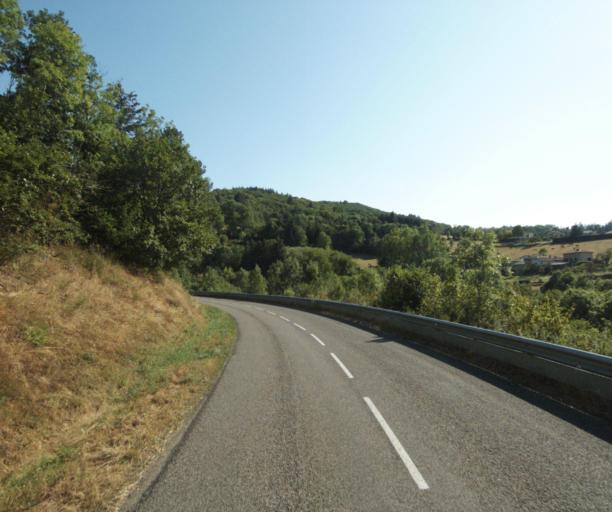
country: FR
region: Rhone-Alpes
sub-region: Departement du Rhone
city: Saint-Pierre-la-Palud
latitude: 45.7712
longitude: 4.6117
